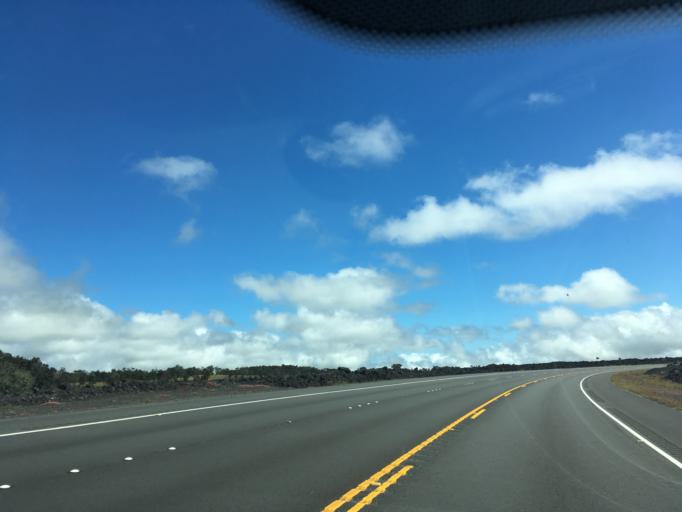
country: US
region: Hawaii
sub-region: Hawaii County
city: Volcano
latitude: 19.6813
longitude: -155.3937
